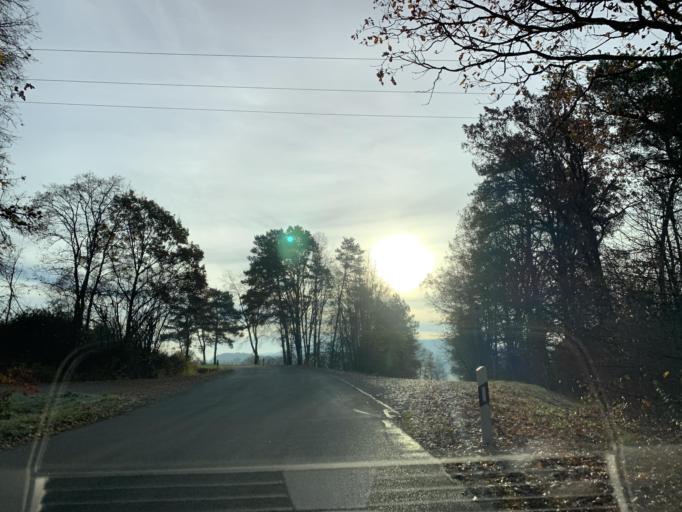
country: DE
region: Bavaria
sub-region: Upper Palatinate
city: Thanstein
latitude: 49.3486
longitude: 12.4378
